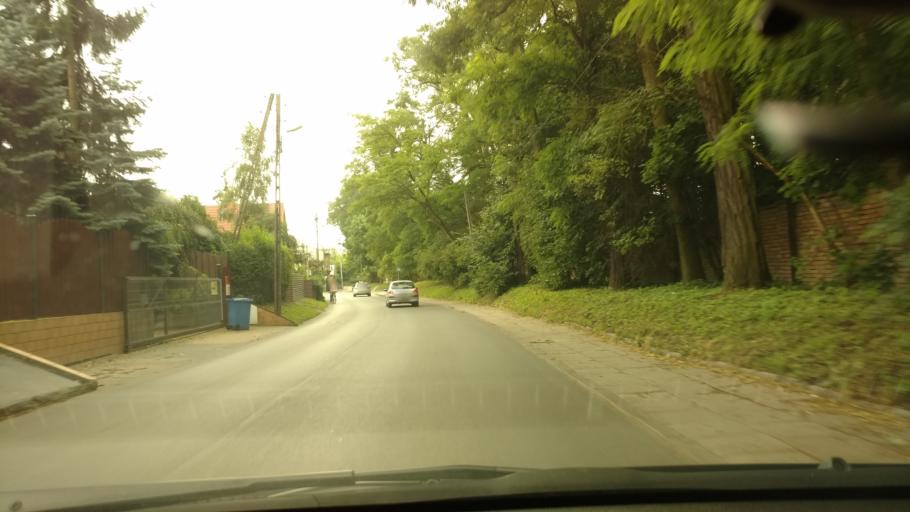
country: PL
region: Lesser Poland Voivodeship
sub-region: Powiat krakowski
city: Zielonki
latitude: 50.0990
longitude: 19.9474
